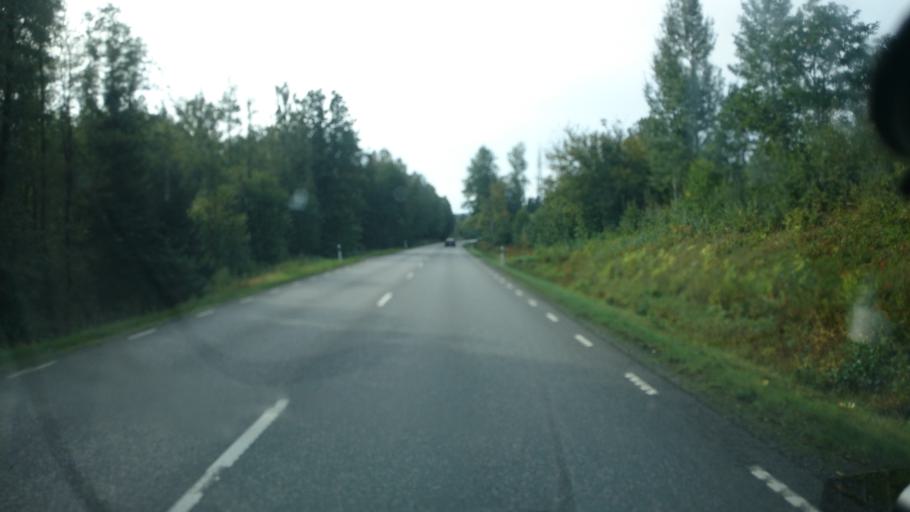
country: SE
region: Vaestra Goetaland
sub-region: Alingsas Kommun
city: Alingsas
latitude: 58.0180
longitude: 12.4539
